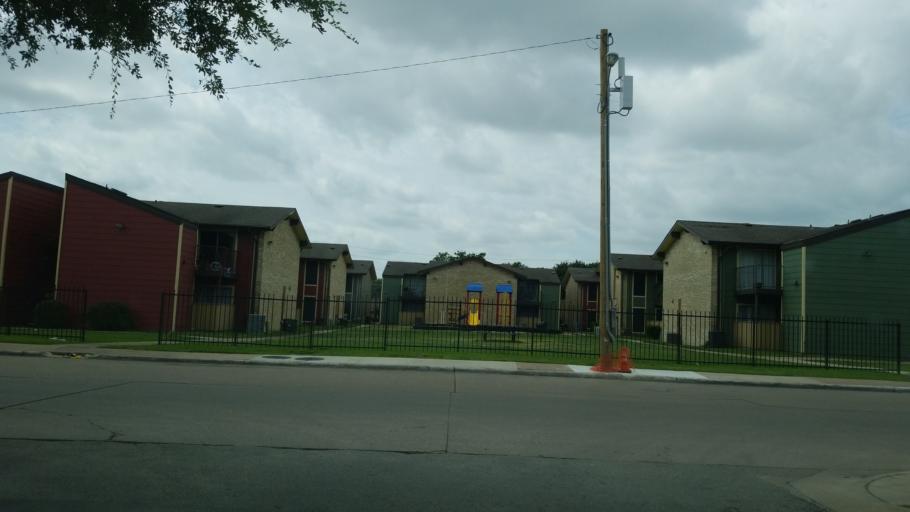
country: US
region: Texas
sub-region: Dallas County
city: Farmers Branch
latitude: 32.8746
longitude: -96.8691
